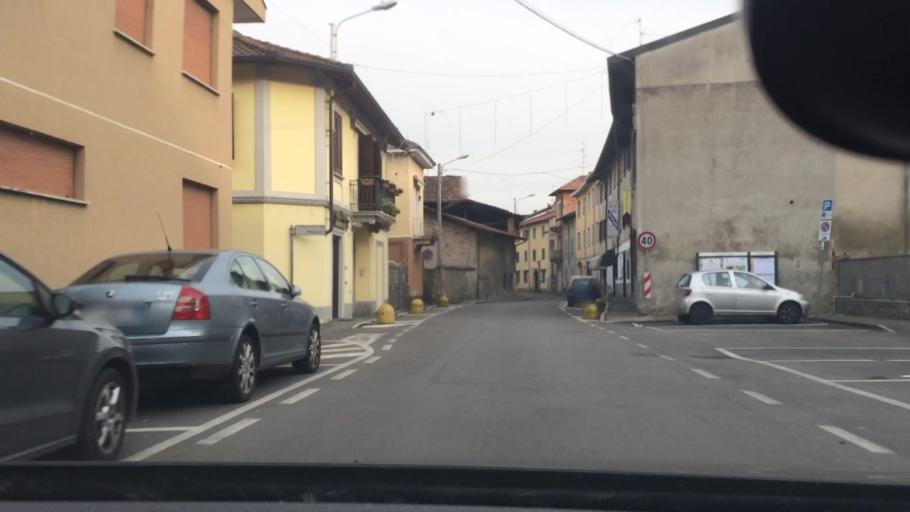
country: IT
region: Lombardy
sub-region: Provincia di Como
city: Rovellasca
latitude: 45.6663
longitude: 9.0517
